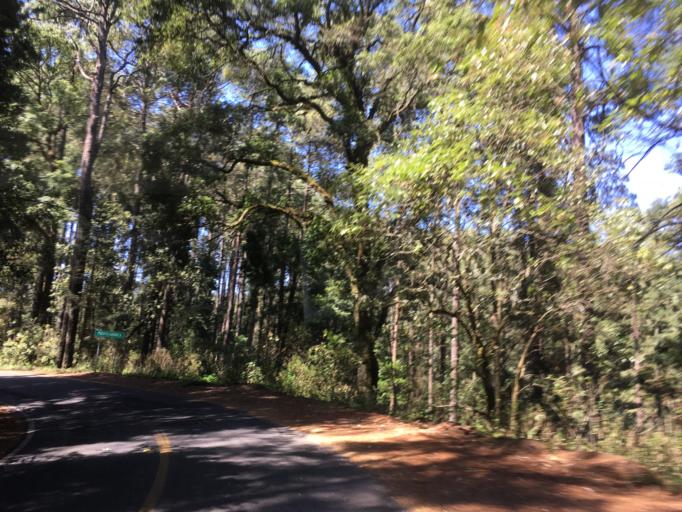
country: MX
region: Michoacan
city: Tzitzio
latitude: 19.6732
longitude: -100.8231
